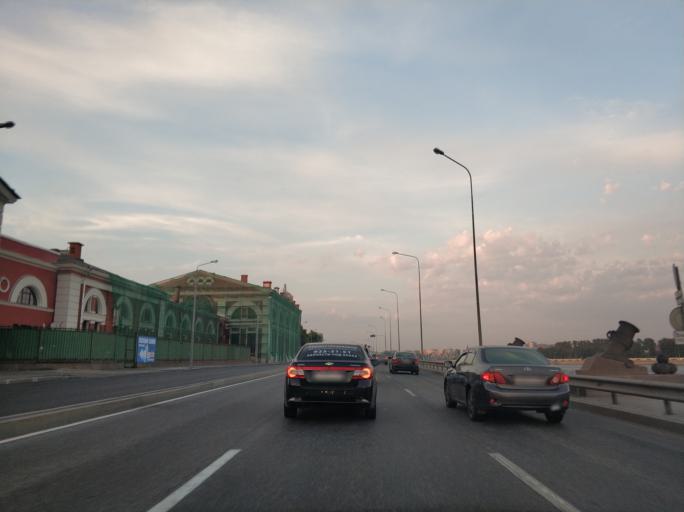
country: RU
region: Leningrad
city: Finlyandskiy
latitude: 59.9536
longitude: 30.3699
